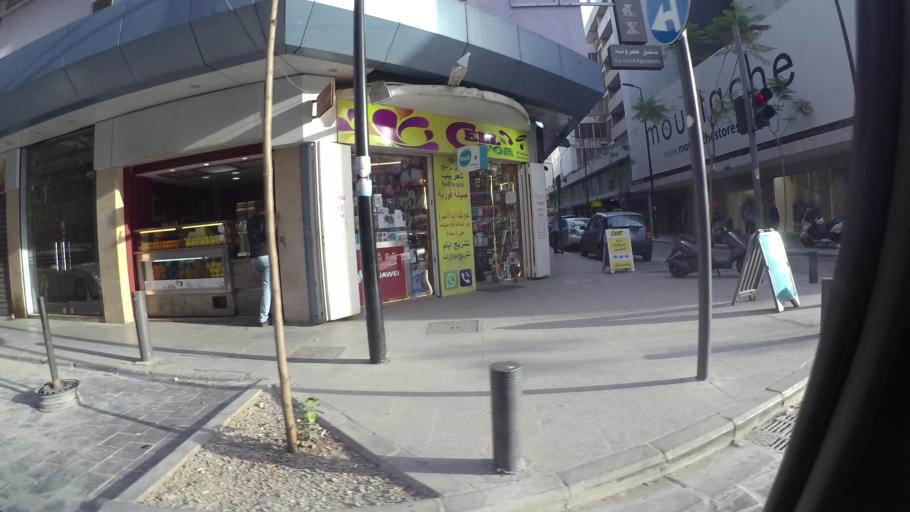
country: LB
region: Beyrouth
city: Ra's Bayrut
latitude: 33.8965
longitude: 35.4814
